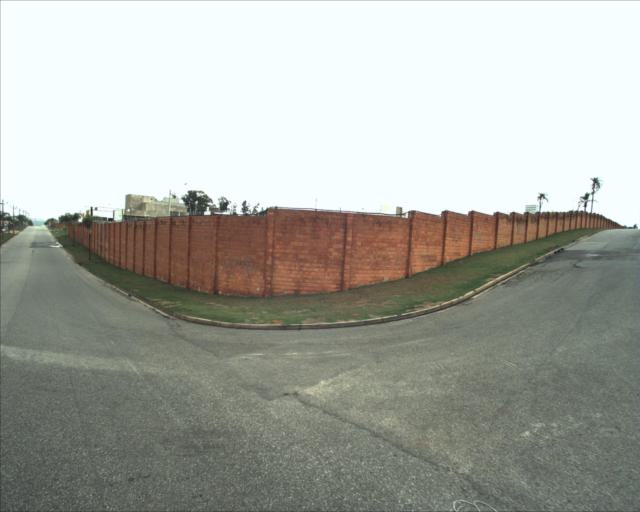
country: BR
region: Sao Paulo
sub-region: Sorocaba
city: Sorocaba
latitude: -23.4460
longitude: -47.4441
